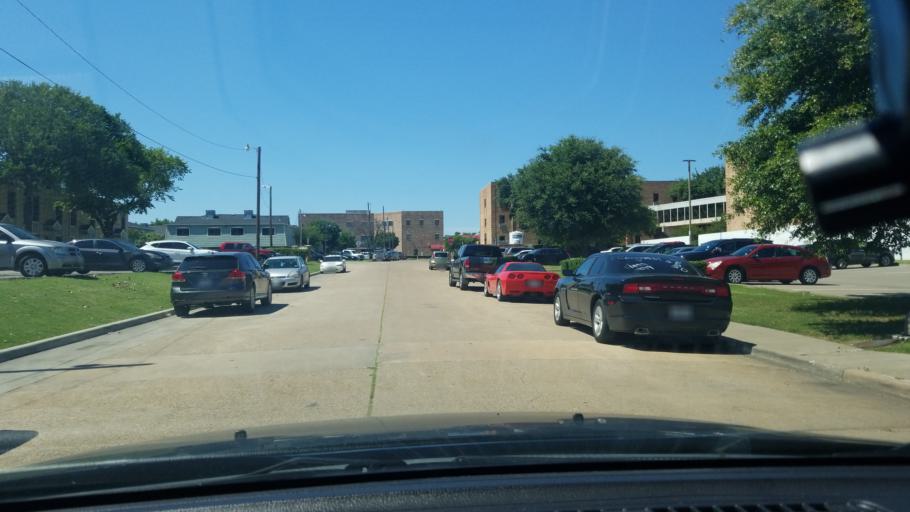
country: US
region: Texas
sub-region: Dallas County
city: Mesquite
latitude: 32.7764
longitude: -96.6009
